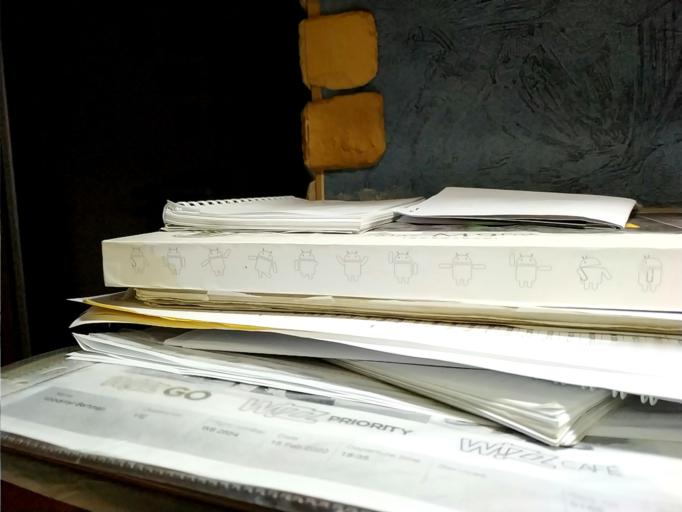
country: RU
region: Arkhangelskaya
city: Onega
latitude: 63.4601
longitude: 38.1691
